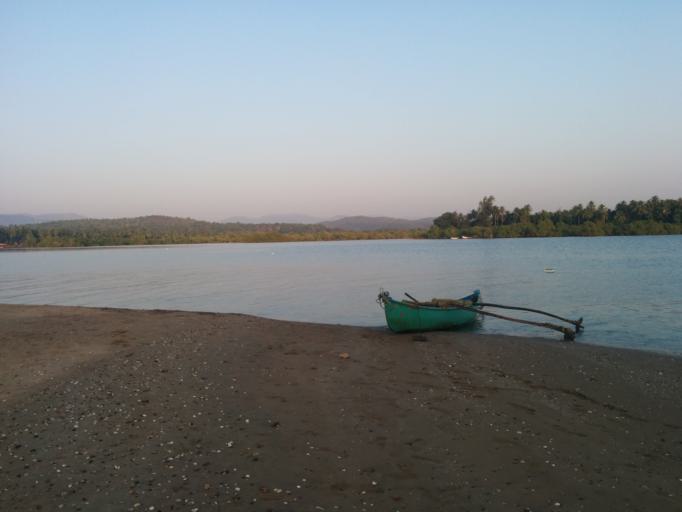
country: IN
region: Karnataka
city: Canacona
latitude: 14.9846
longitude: 74.0389
